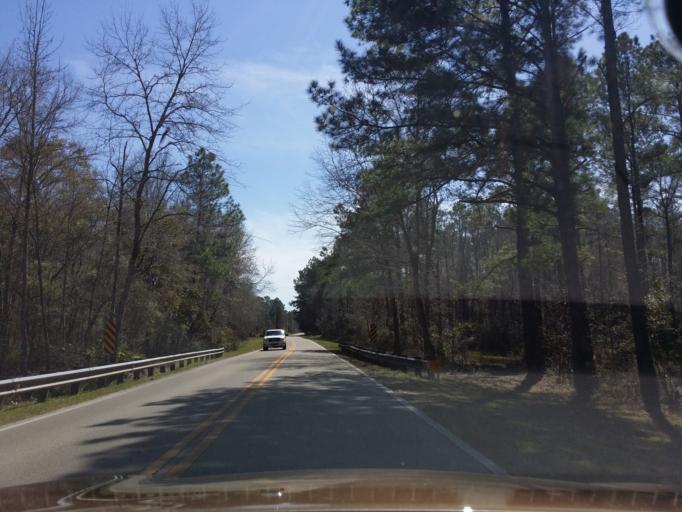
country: US
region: Florida
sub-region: Leon County
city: Woodville
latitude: 30.3045
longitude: -84.1586
